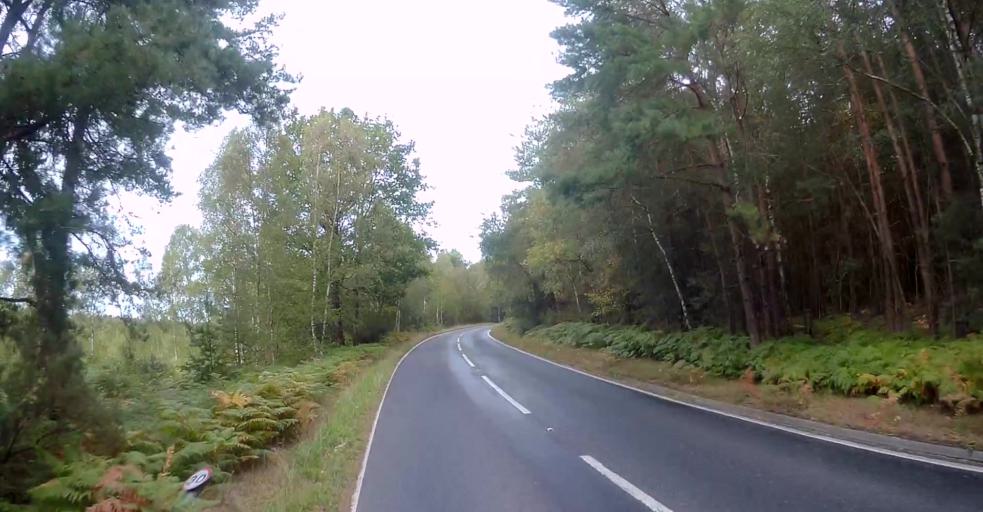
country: GB
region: England
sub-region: Surrey
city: Normandy
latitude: 51.2881
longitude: -0.6917
